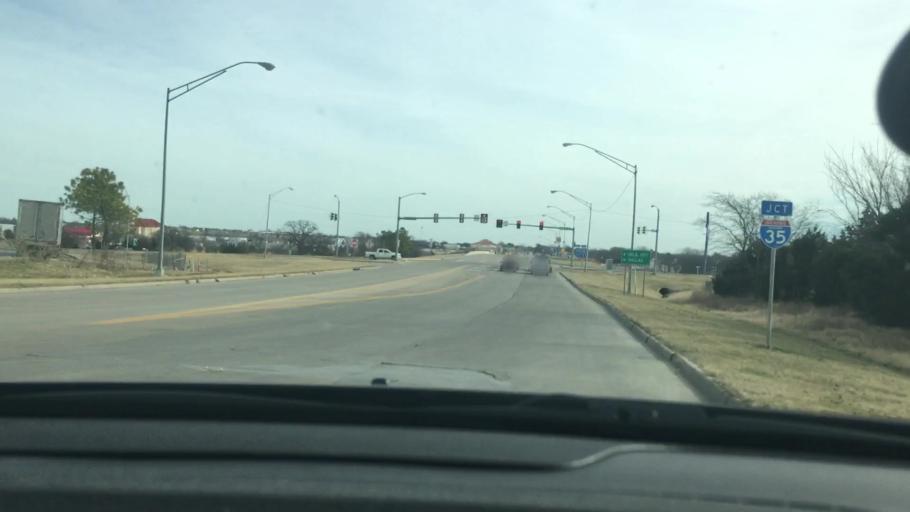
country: US
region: Oklahoma
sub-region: Carter County
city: Ardmore
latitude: 34.1874
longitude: -97.1703
